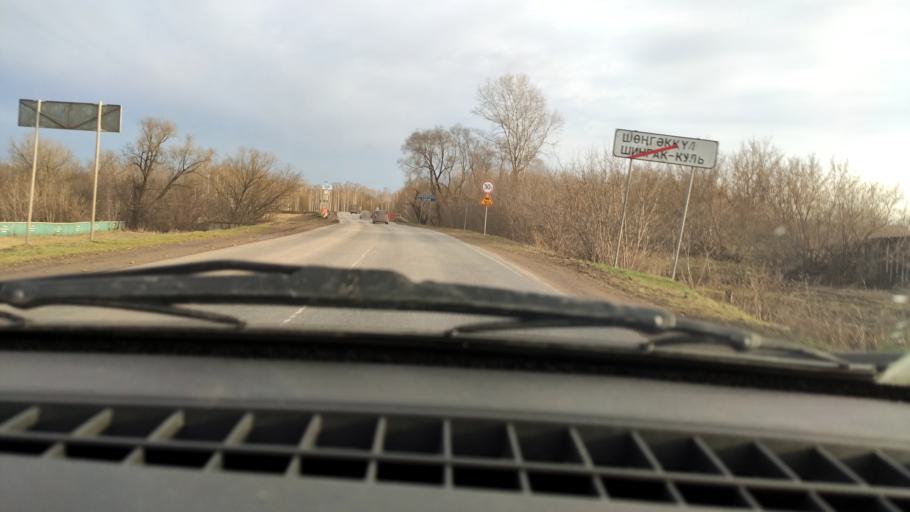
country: RU
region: Bashkortostan
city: Davlekanovo
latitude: 54.3669
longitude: 55.1952
